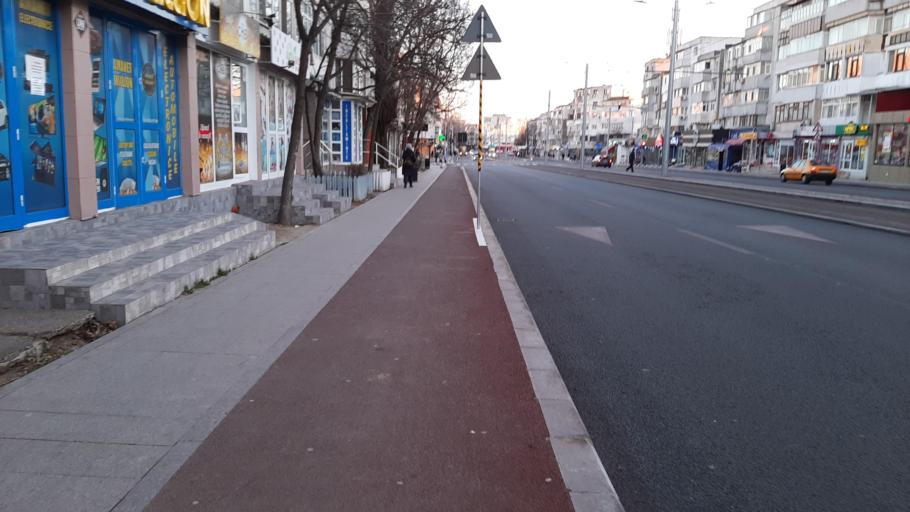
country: RO
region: Galati
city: Galati
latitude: 45.4377
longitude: 28.0231
